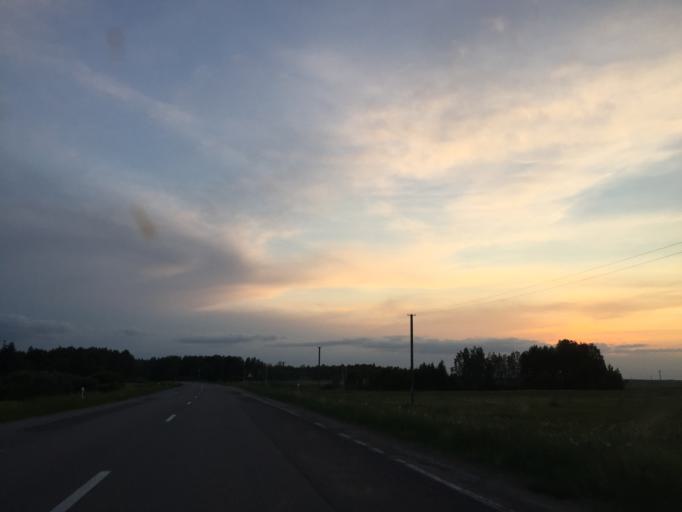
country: LT
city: Venta
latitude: 56.0060
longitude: 22.7082
